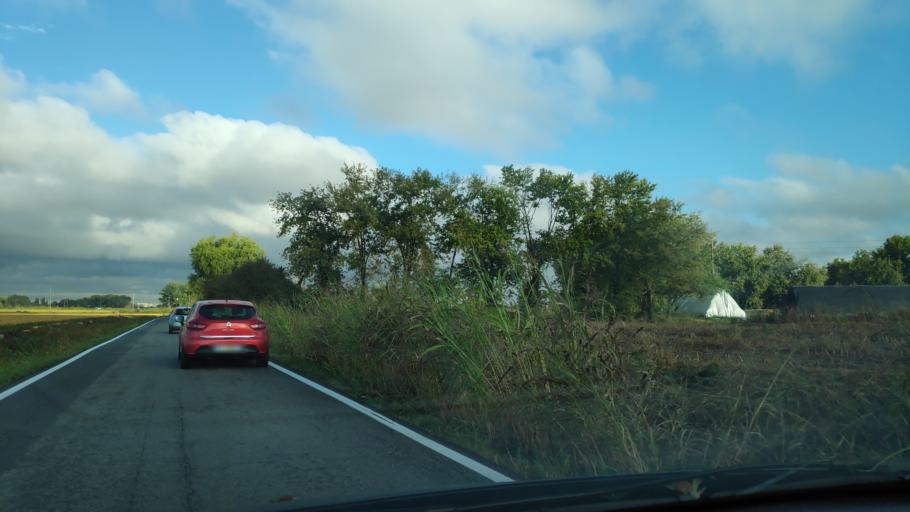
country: IT
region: Lombardy
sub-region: Citta metropolitana di Milano
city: Opera
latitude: 45.3831
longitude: 9.2064
